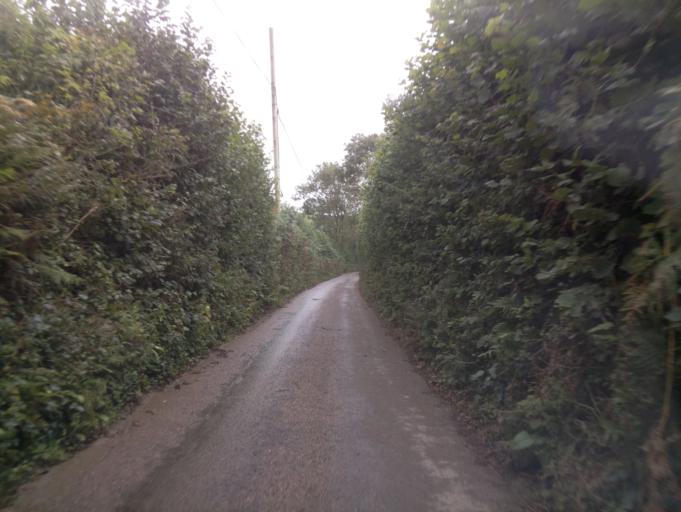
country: GB
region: England
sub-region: Devon
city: Totnes
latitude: 50.3409
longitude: -3.6846
